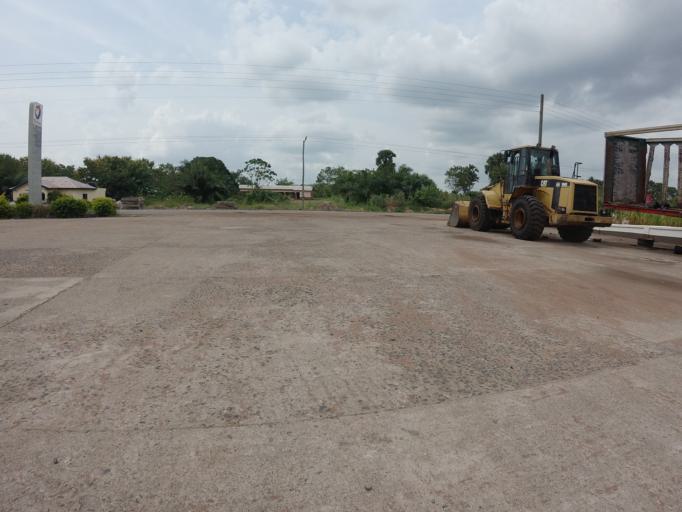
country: GH
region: Volta
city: Ho
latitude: 6.5736
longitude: 0.3751
